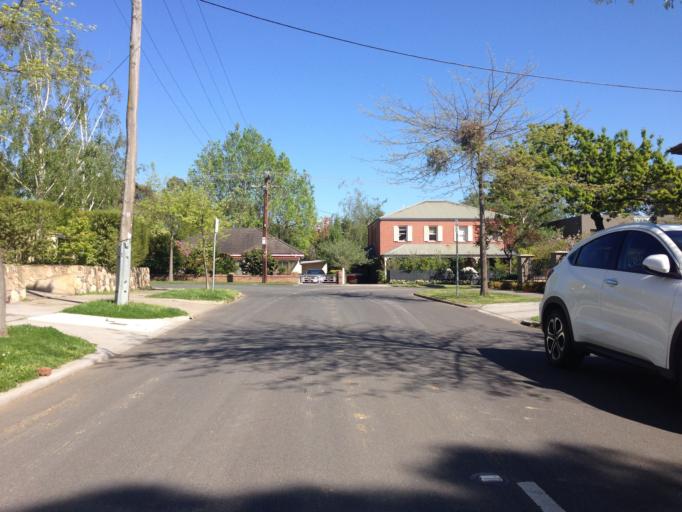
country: AU
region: Victoria
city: Balwyn
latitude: -37.8060
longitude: 145.0679
